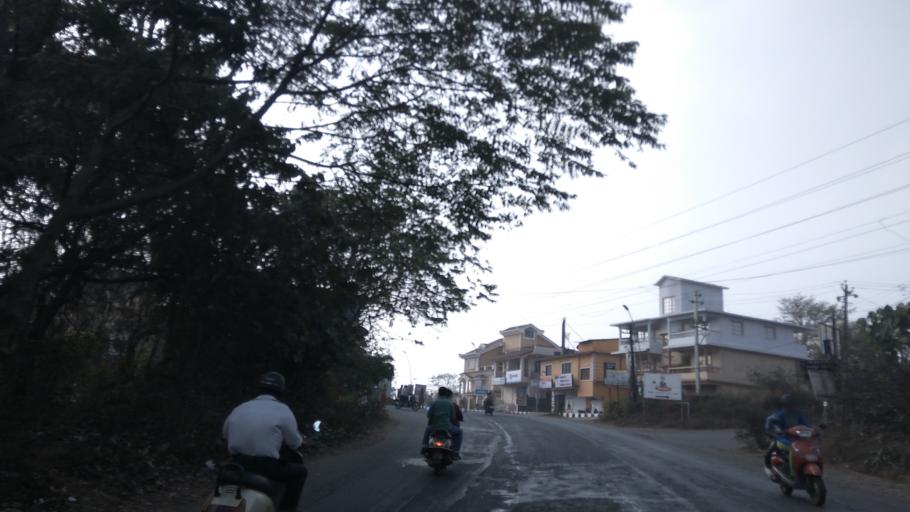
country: IN
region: Goa
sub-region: North Goa
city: Serula
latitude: 15.5404
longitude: 73.8167
